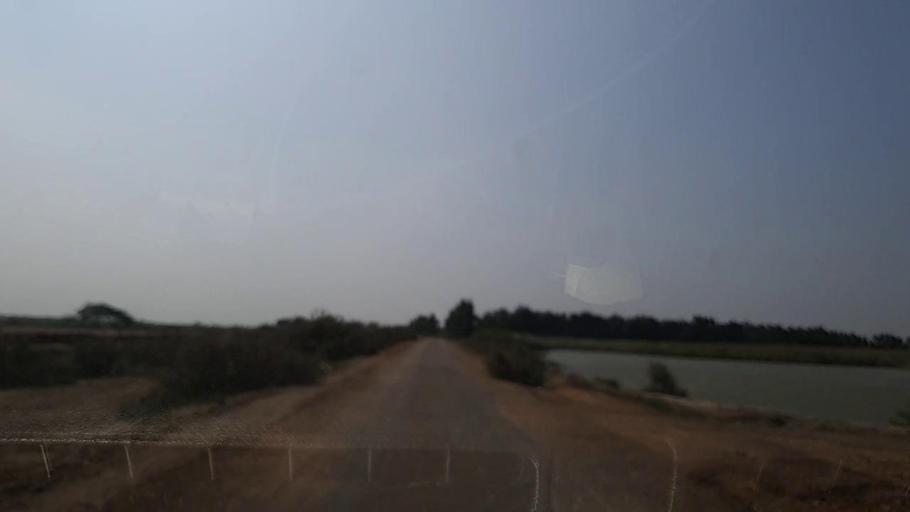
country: PK
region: Sindh
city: Mirpur Sakro
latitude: 24.5284
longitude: 67.7766
